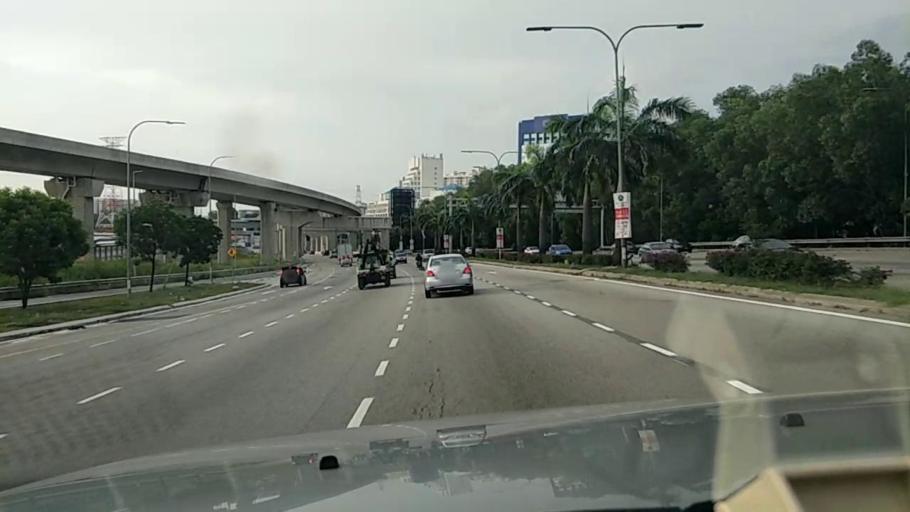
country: MY
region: Selangor
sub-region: Petaling
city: Petaling Jaya
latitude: 3.0921
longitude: 101.5915
